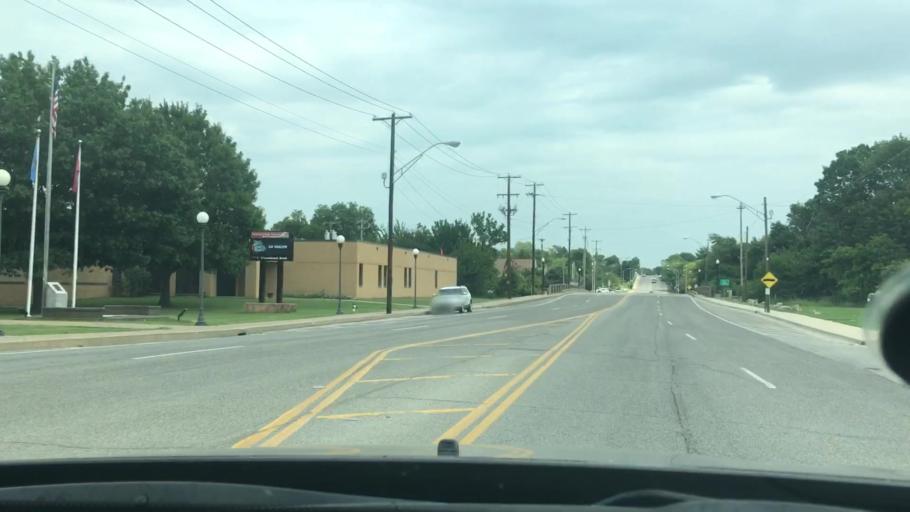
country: US
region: Oklahoma
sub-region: Murray County
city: Sulphur
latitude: 34.5064
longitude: -96.9777
